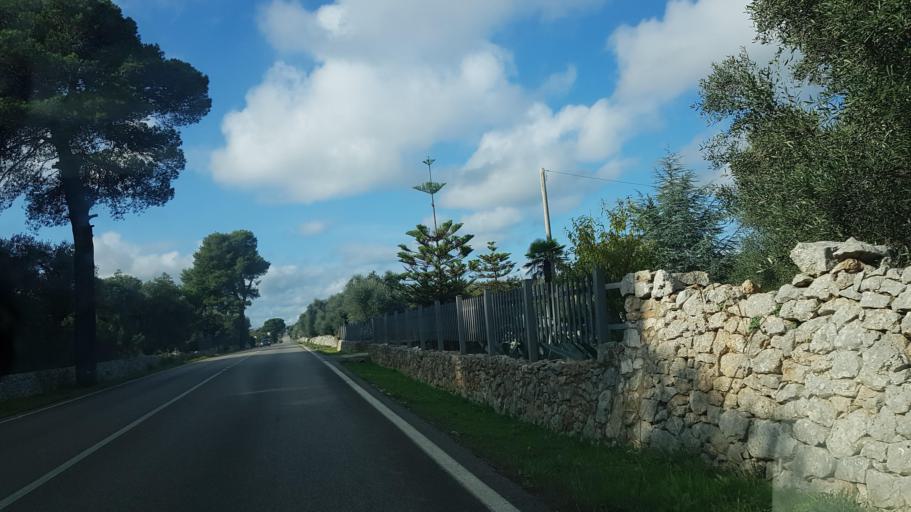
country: IT
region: Apulia
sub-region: Provincia di Brindisi
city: Carovigno
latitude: 40.7111
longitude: 17.6351
